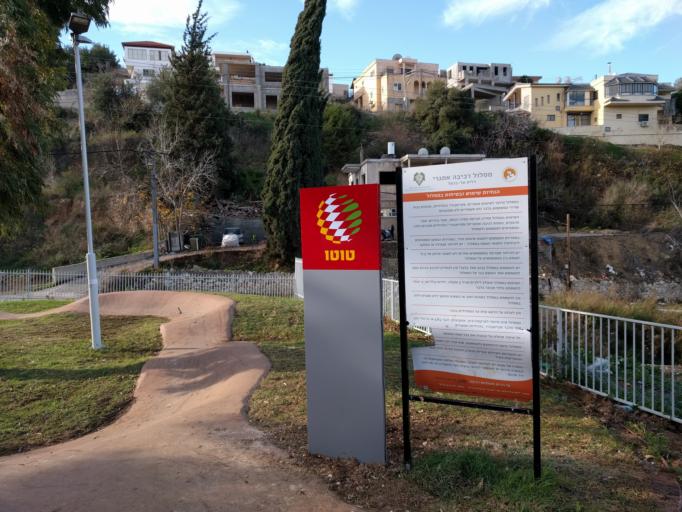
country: IL
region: Haifa
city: Daliyat el Karmil
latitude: 32.6960
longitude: 35.0393
